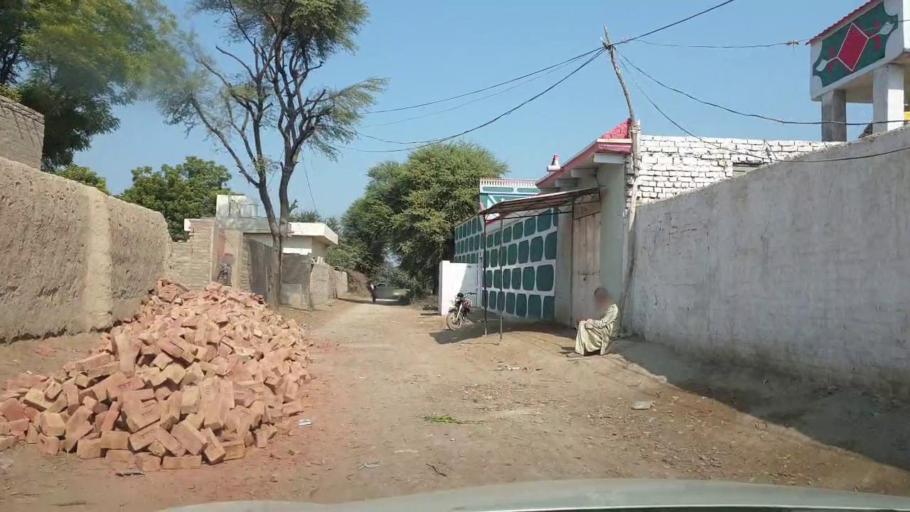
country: PK
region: Sindh
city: Bhit Shah
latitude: 25.7481
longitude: 68.4791
